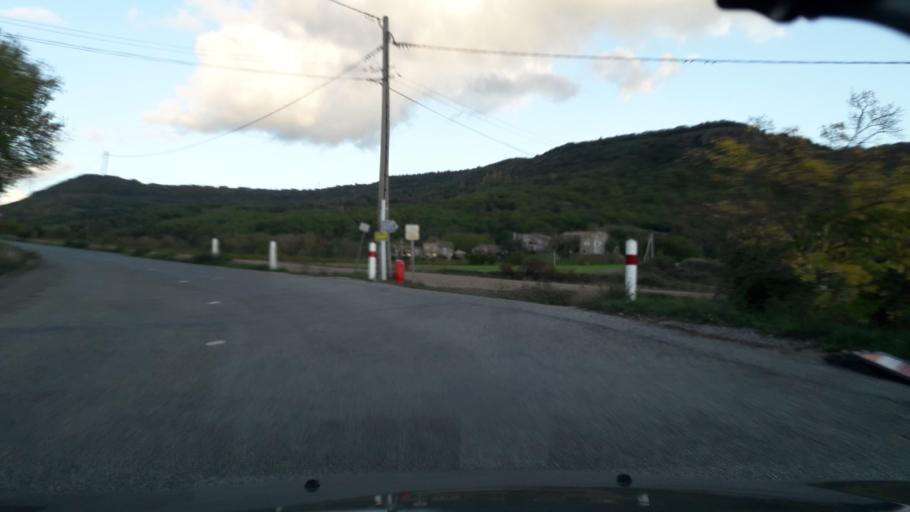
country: FR
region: Rhone-Alpes
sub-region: Departement de l'Ardeche
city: Vesseaux
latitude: 44.6270
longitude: 4.4883
